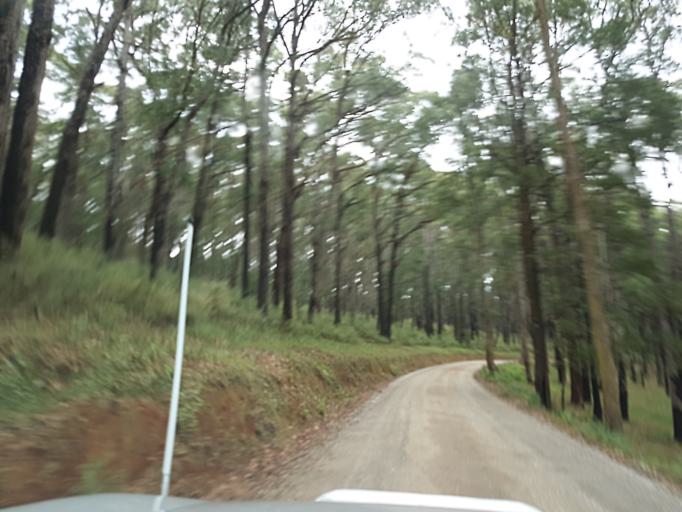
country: AU
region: Victoria
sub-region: Yarra Ranges
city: Olinda
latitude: -37.8470
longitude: 145.3949
